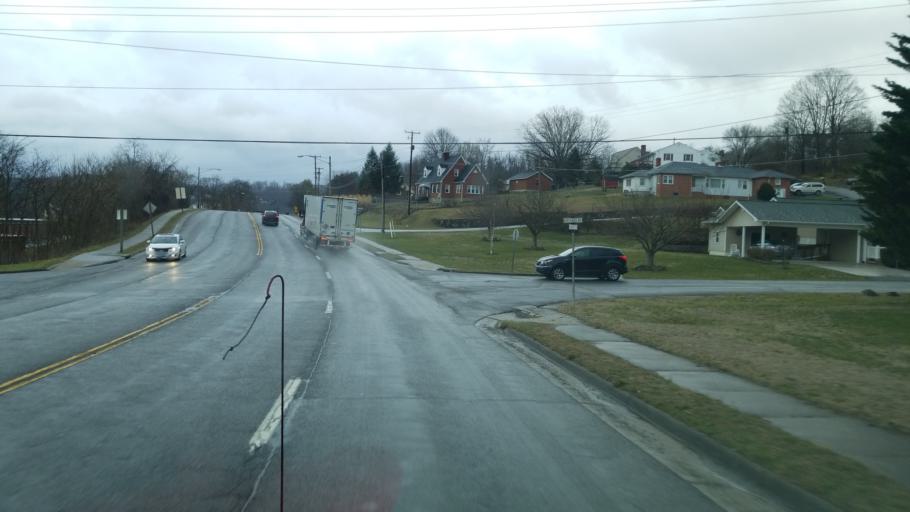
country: US
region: Virginia
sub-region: Giles County
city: Pearisburg
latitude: 37.3242
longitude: -80.7339
